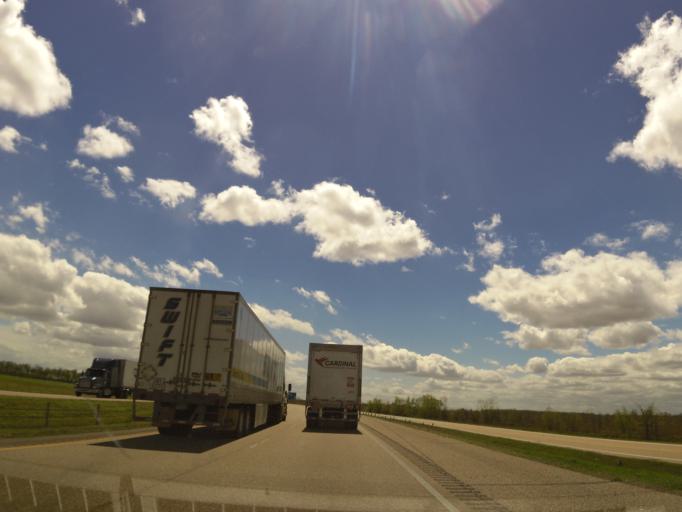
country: US
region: Arkansas
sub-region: Crittenden County
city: Marion
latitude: 35.3869
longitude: -90.2791
